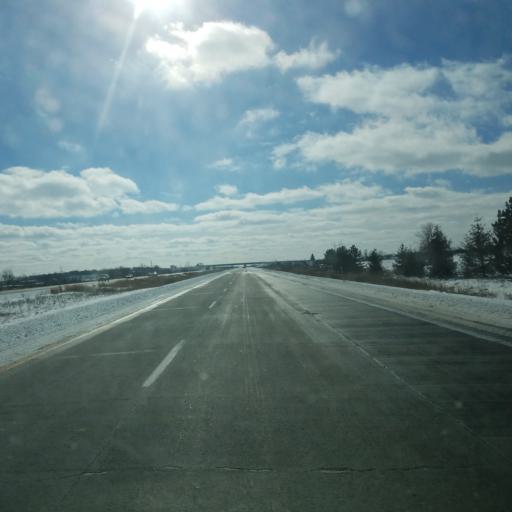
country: US
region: Michigan
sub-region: Clinton County
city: Saint Johns
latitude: 42.9942
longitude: -84.5191
